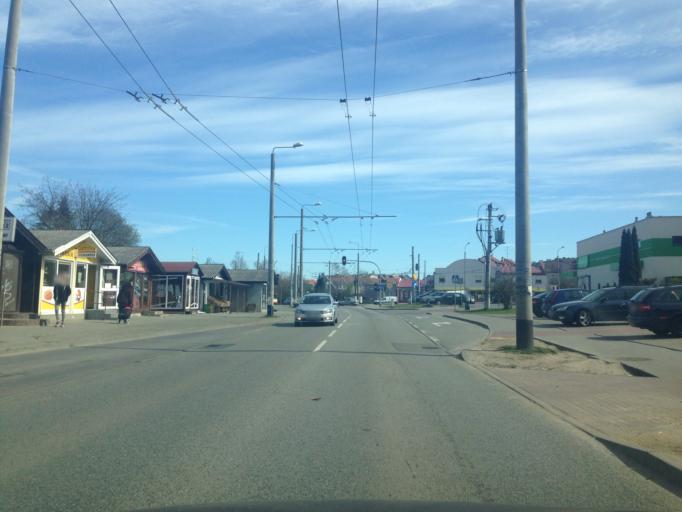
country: PL
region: Pomeranian Voivodeship
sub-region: Gdynia
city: Wielki Kack
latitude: 54.4745
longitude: 18.4639
